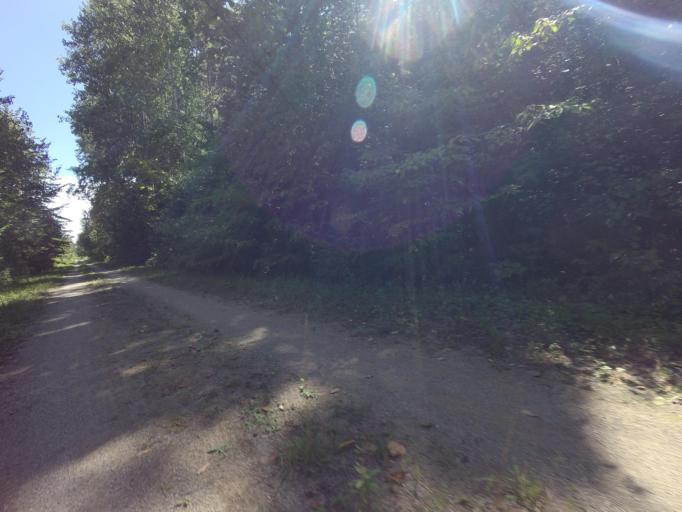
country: CA
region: Ontario
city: Orangeville
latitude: 43.7777
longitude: -80.2065
